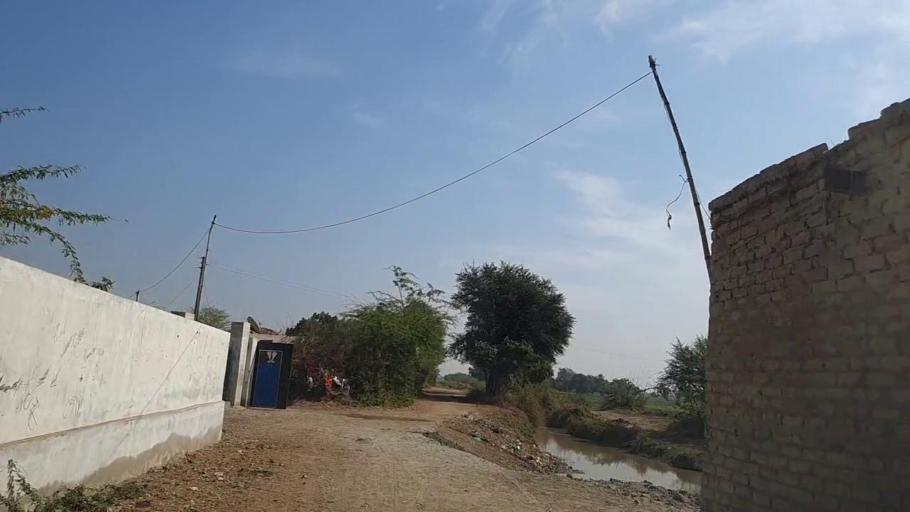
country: PK
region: Sindh
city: Mirpur Khas
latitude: 25.4691
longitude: 68.9762
